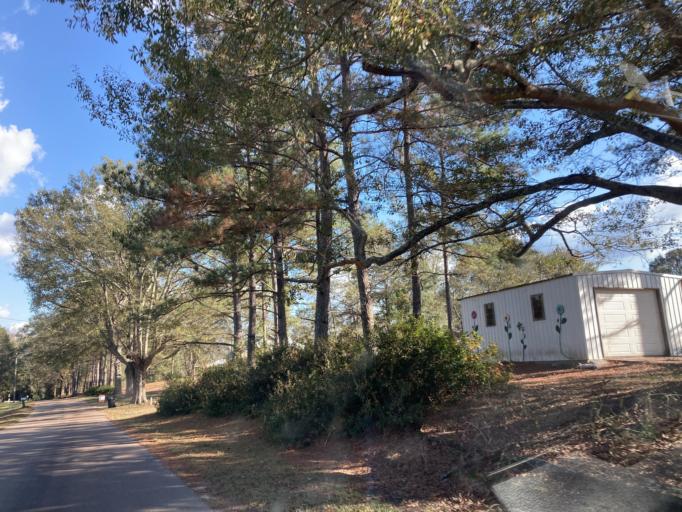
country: US
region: Mississippi
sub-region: Lamar County
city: Sumrall
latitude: 31.4205
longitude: -89.6361
